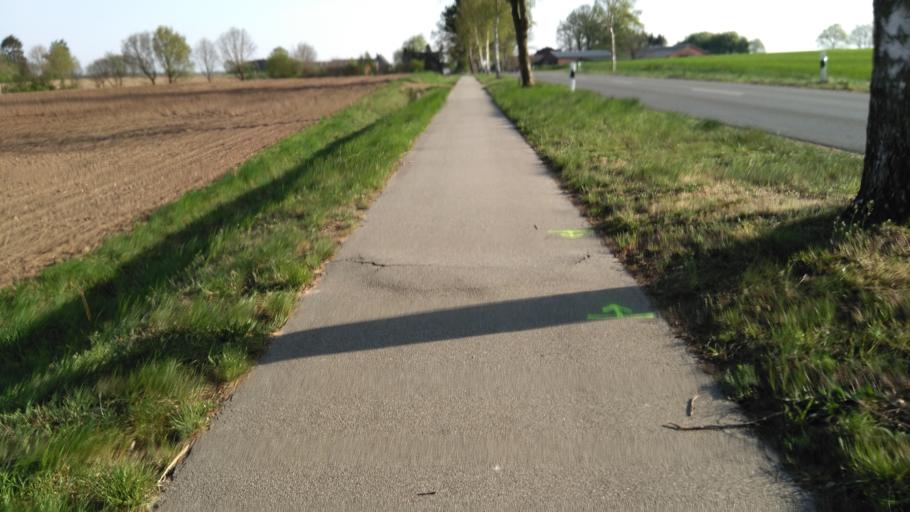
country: DE
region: Lower Saxony
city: Apensen
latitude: 53.4307
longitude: 9.6563
